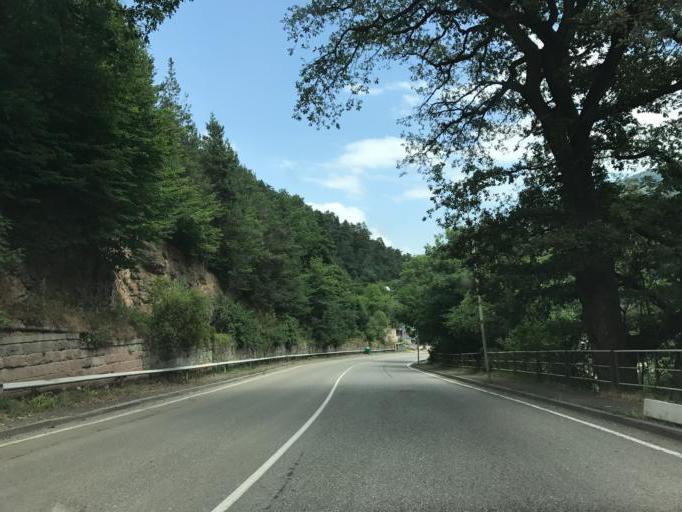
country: AM
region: Tavush
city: Dilijan
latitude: 40.7233
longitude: 44.8591
